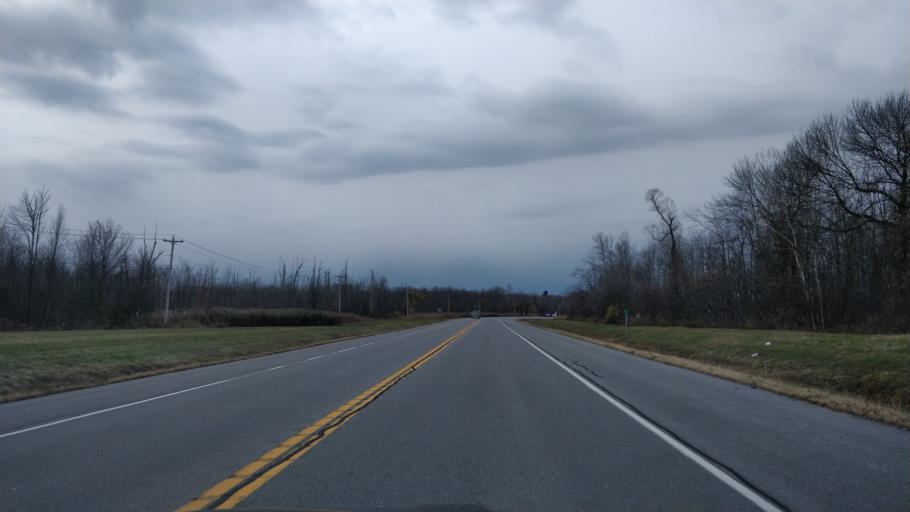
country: US
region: New York
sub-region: St. Lawrence County
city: Ogdensburg
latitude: 44.7089
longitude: -75.4517
